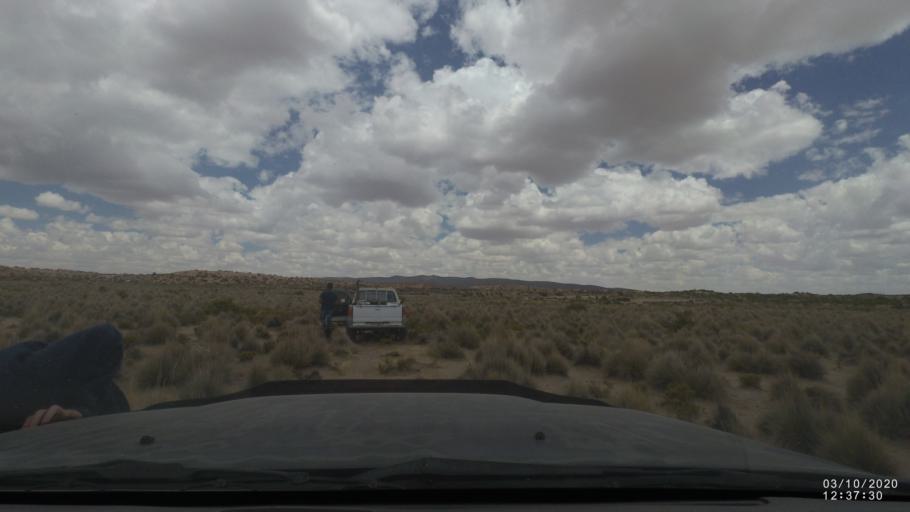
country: BO
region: Oruro
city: Poopo
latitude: -18.6881
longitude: -67.5358
